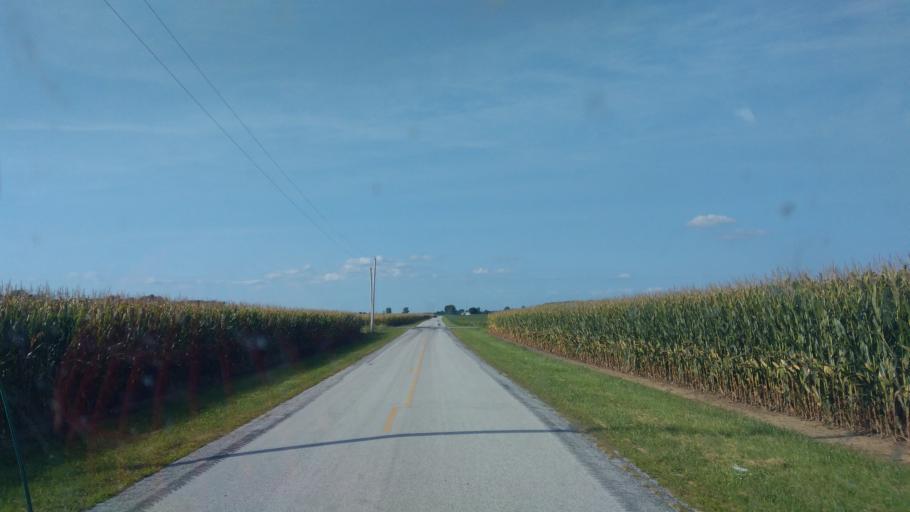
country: US
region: Ohio
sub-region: Hardin County
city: Kenton
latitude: 40.7160
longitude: -83.5725
